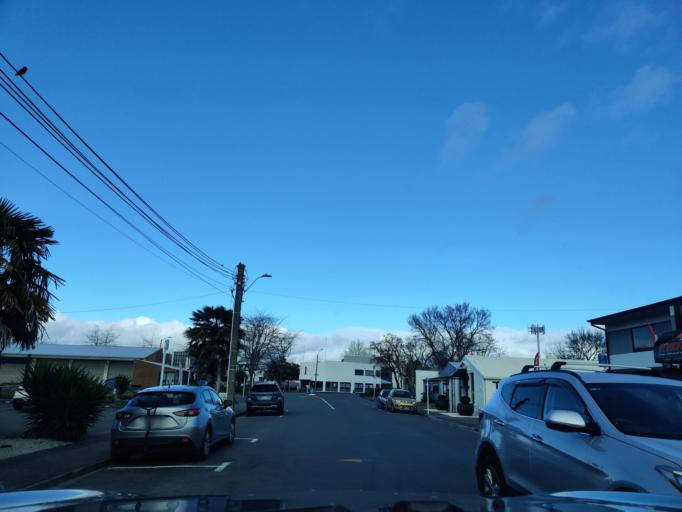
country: NZ
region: Hawke's Bay
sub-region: Hastings District
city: Hastings
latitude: -39.6678
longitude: 176.8779
